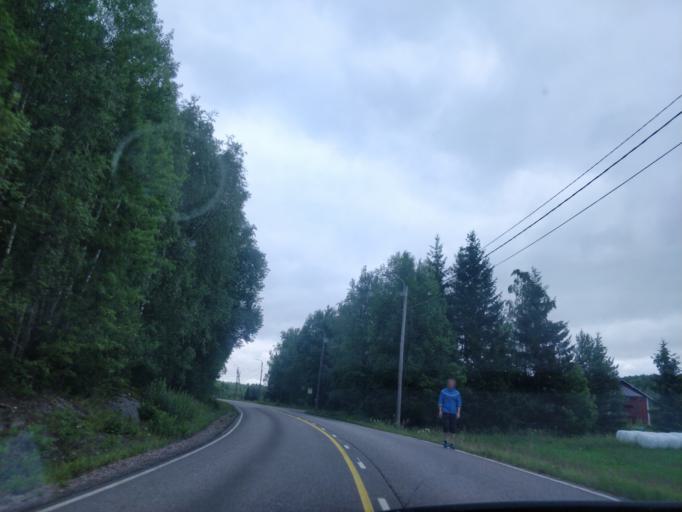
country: FI
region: Uusimaa
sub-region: Helsinki
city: Kauniainen
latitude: 60.2785
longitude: 24.7128
